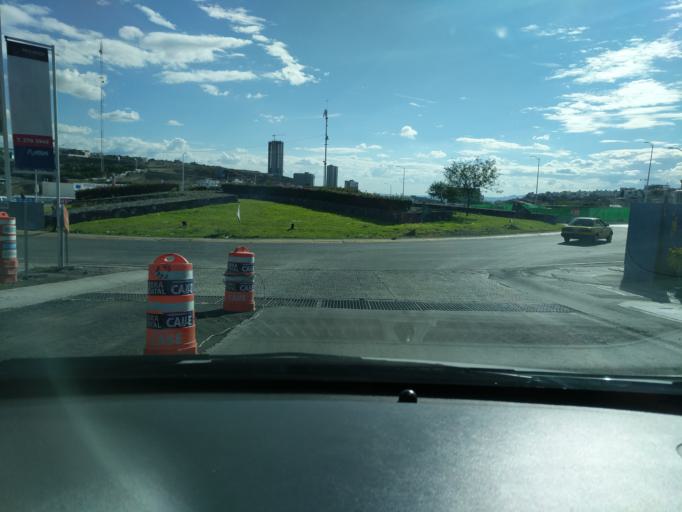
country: MX
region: Queretaro
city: La Canada
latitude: 20.5902
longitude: -100.3371
